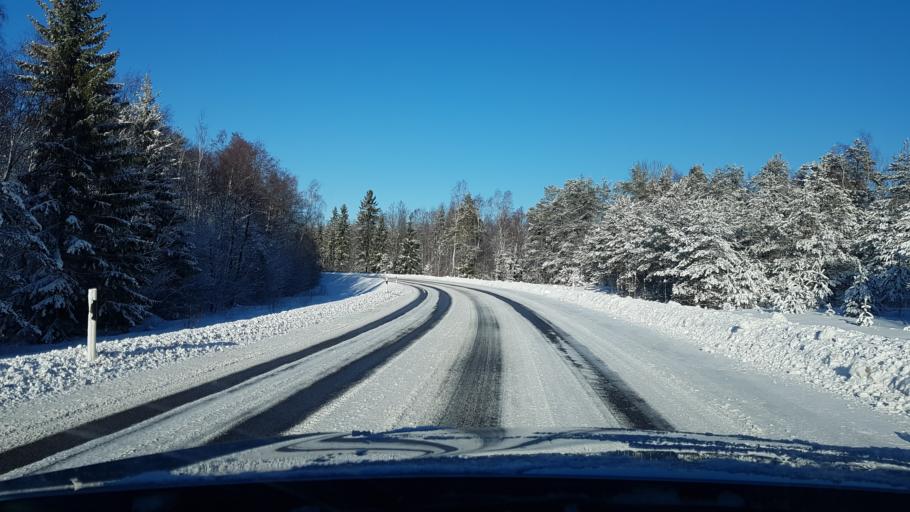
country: EE
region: Hiiumaa
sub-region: Kaerdla linn
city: Kardla
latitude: 58.9655
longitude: 22.7730
